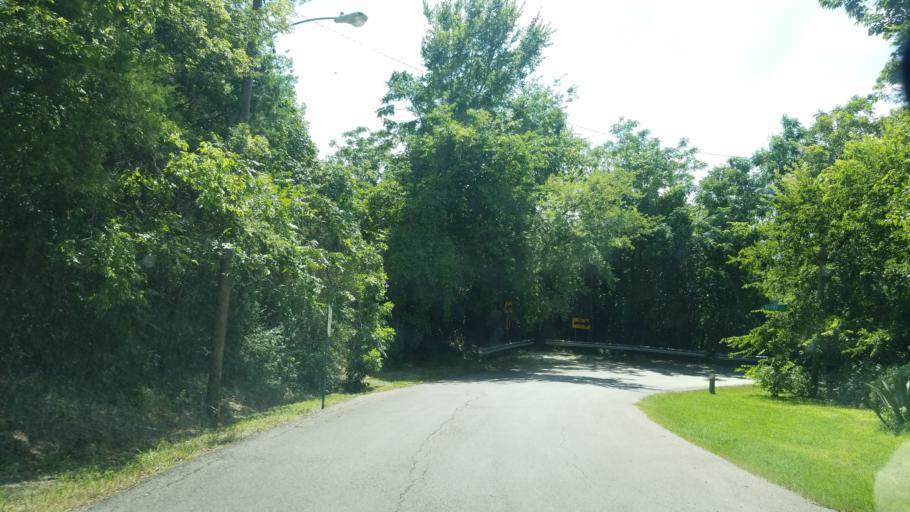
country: US
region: Texas
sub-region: Dallas County
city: Balch Springs
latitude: 32.7614
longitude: -96.7042
